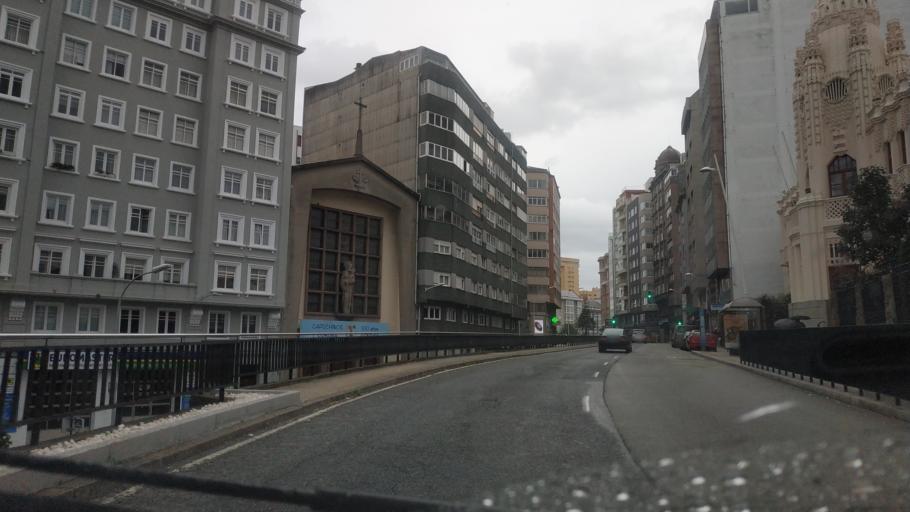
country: ES
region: Galicia
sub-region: Provincia da Coruna
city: A Coruna
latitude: 43.3608
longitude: -8.4068
